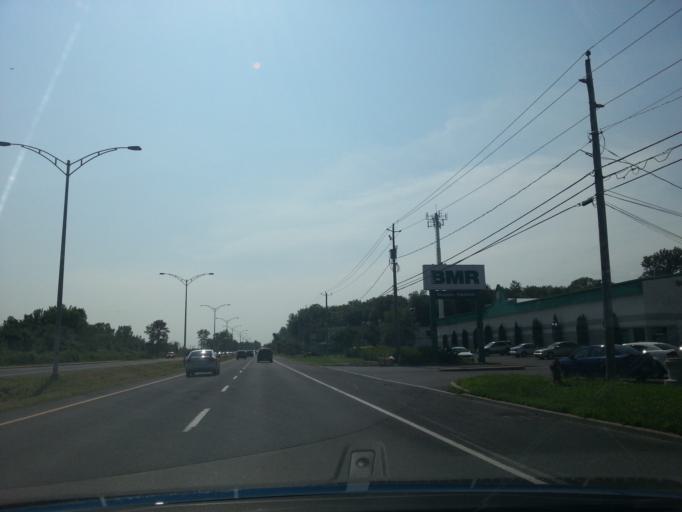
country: CA
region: Quebec
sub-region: Monteregie
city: Saint-Basile-le-Grand
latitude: 45.5241
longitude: -73.3052
